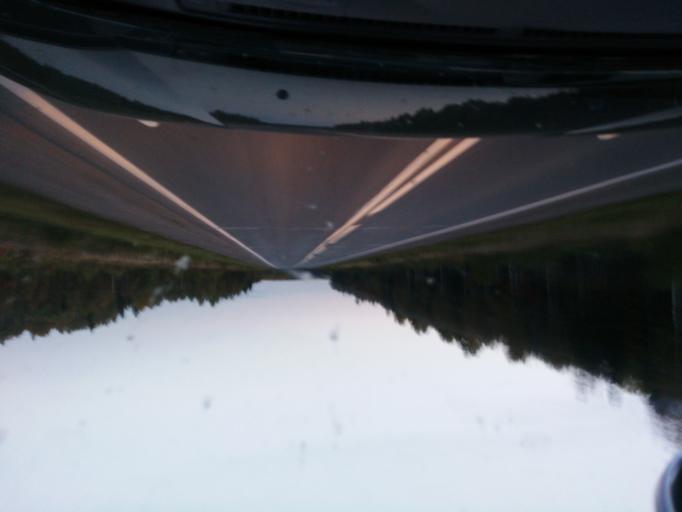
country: RU
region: Perm
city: Verkhnechusovskiye Gorodki
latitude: 58.2308
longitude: 57.2101
